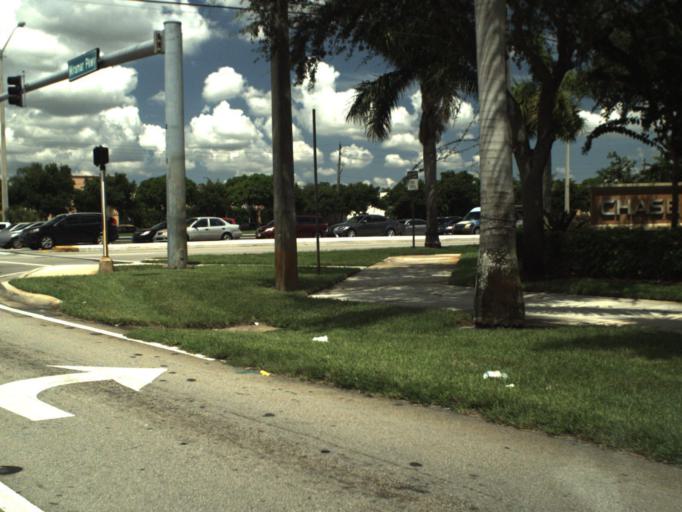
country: US
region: Florida
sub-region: Miami-Dade County
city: Lake Lucerne
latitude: 25.9807
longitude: -80.2784
